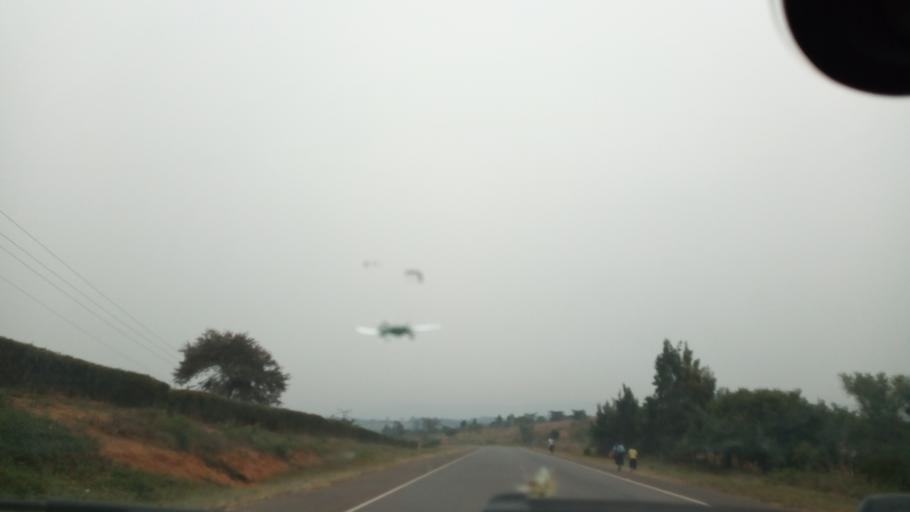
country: UG
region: Western Region
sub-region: Mbarara District
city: Mbarara
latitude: -0.7026
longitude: 30.7065
